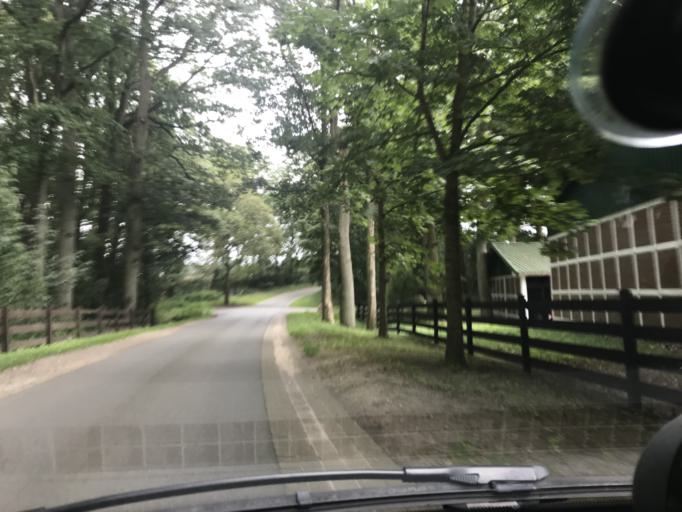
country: DE
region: Lower Saxony
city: Moisburg
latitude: 53.3973
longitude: 9.7231
